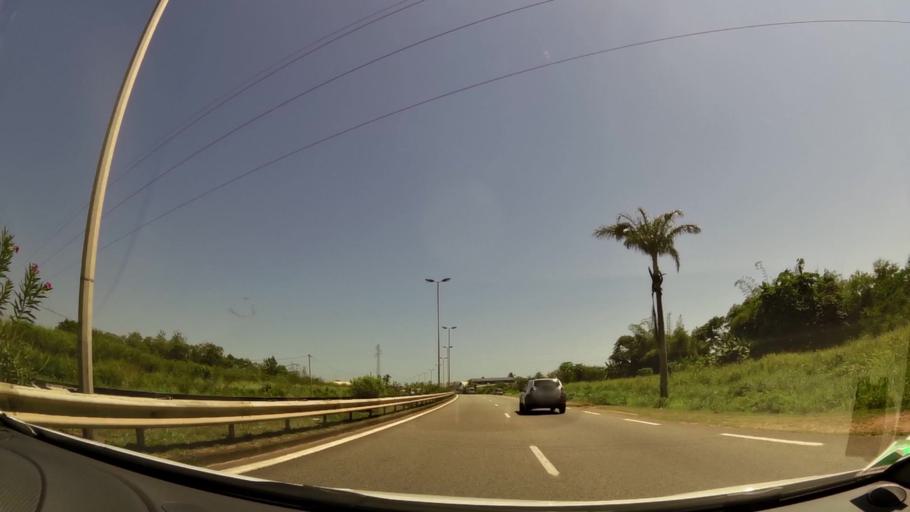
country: GF
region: Guyane
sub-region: Guyane
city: Cayenne
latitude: 4.9269
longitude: -52.3288
